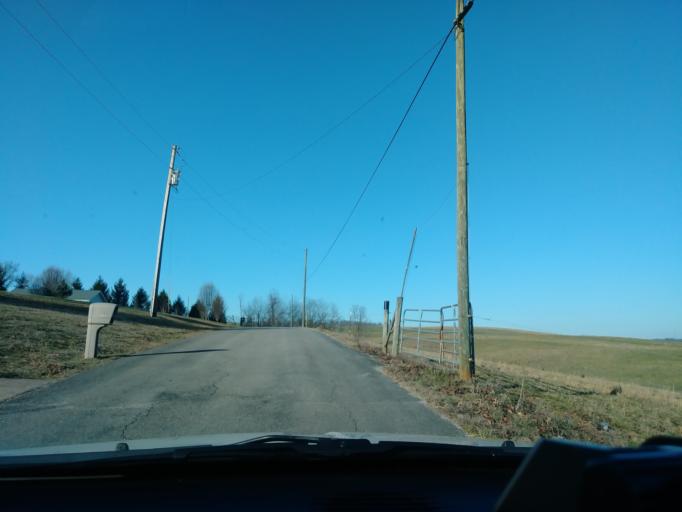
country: US
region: Tennessee
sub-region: Greene County
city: Greeneville
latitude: 36.0765
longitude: -82.9035
